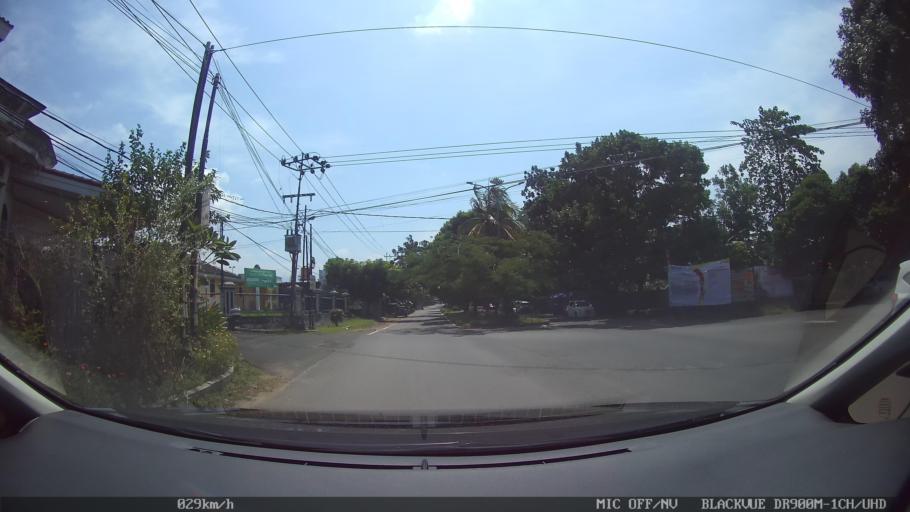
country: ID
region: Lampung
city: Kedaton
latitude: -5.3838
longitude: 105.2742
